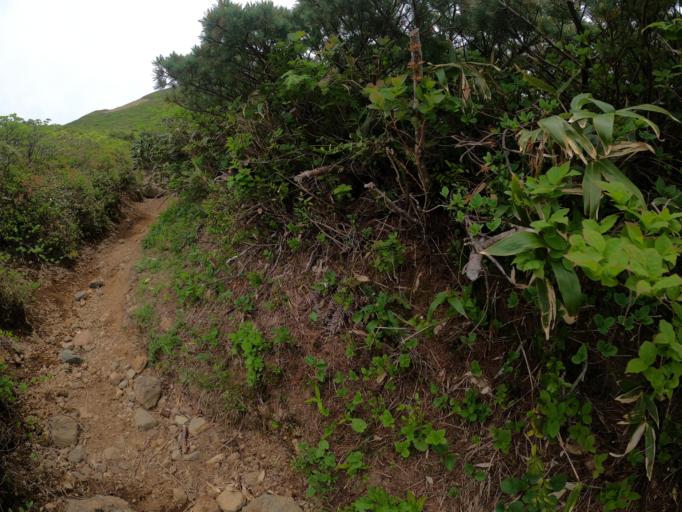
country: JP
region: Iwate
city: Ichinoseki
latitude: 38.9628
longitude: 140.7921
